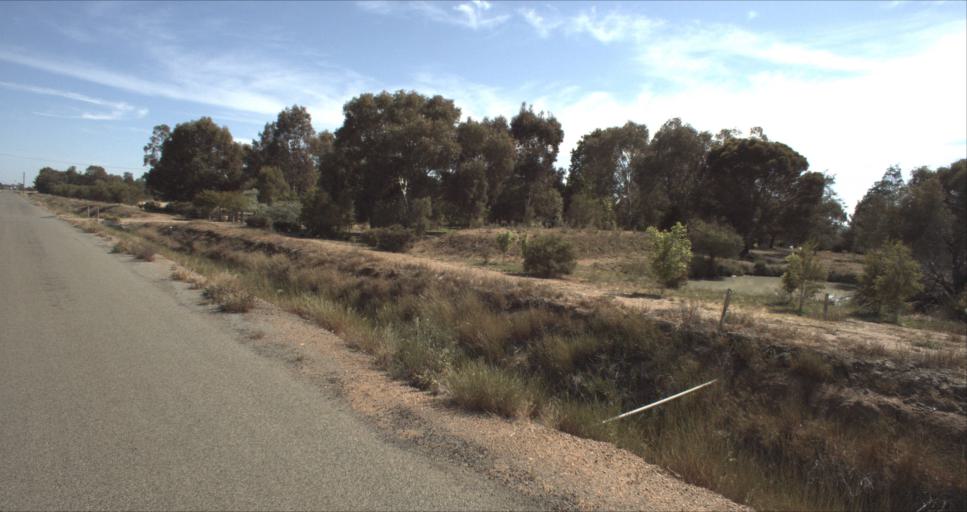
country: AU
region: New South Wales
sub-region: Leeton
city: Leeton
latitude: -34.5750
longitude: 146.4765
